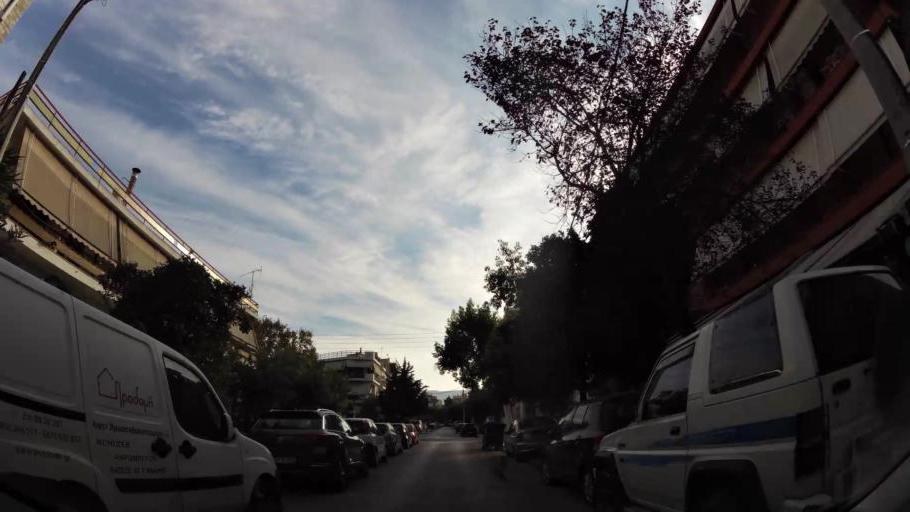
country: GR
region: Attica
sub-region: Nomarchia Athinas
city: Palaio Faliro
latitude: 37.9344
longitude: 23.6994
